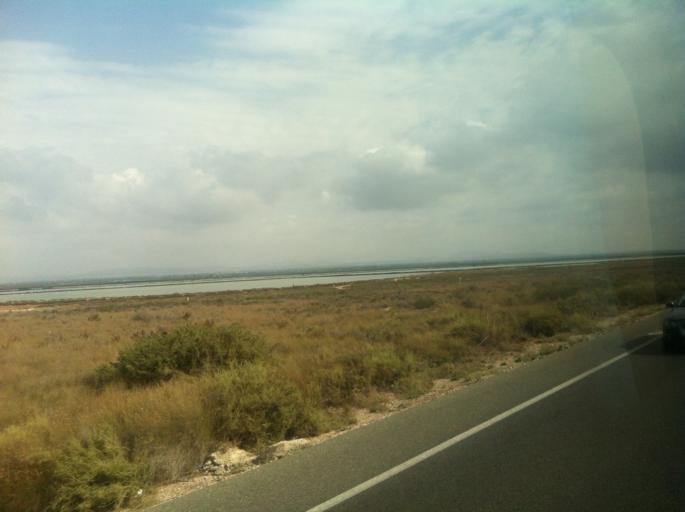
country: ES
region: Valencia
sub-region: Provincia de Alicante
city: Santa Pola
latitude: 38.1656
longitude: -0.6312
